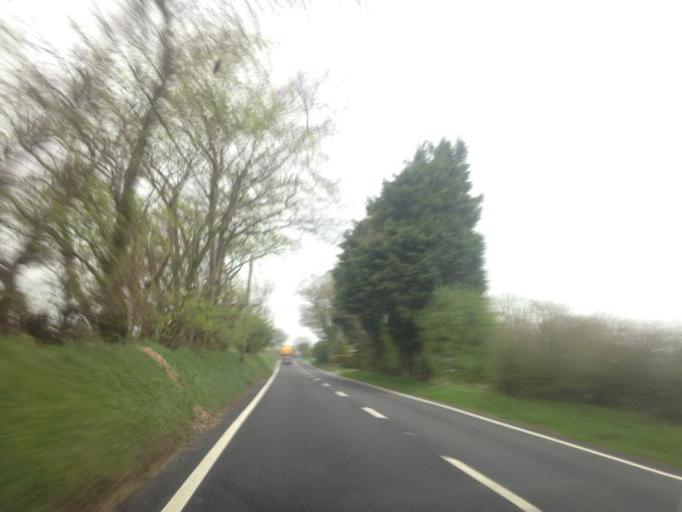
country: GB
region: Wales
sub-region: County of Ceredigion
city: Llanllwchaiarn
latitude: 52.1428
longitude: -4.4000
